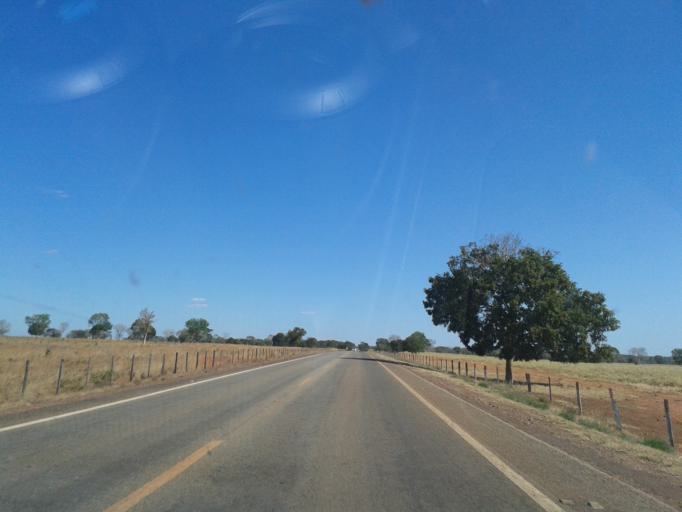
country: BR
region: Goias
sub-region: Crixas
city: Crixas
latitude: -14.1612
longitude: -50.3657
